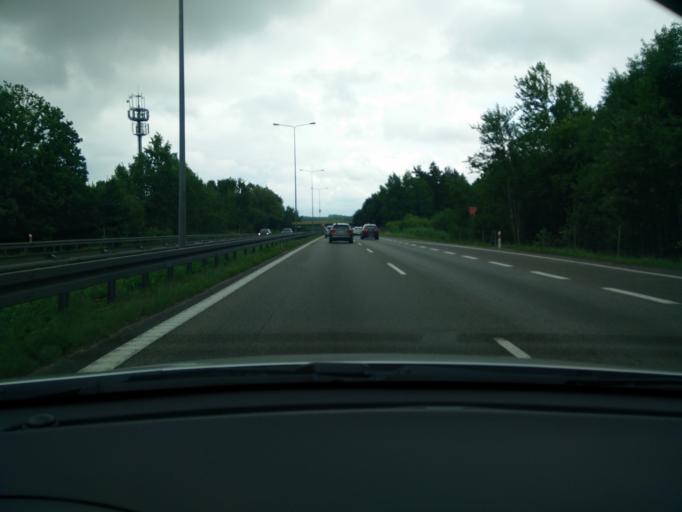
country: PL
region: Pomeranian Voivodeship
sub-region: Gdynia
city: Wielki Kack
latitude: 54.4666
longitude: 18.4795
